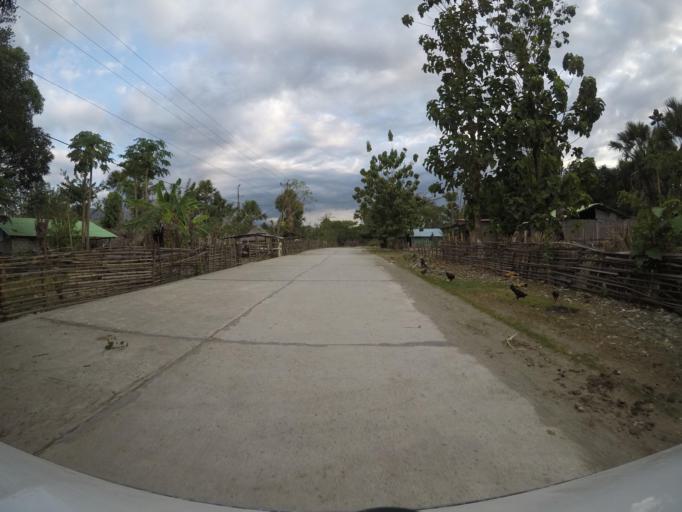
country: TL
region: Bobonaro
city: Maliana
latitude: -8.8723
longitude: 125.2124
